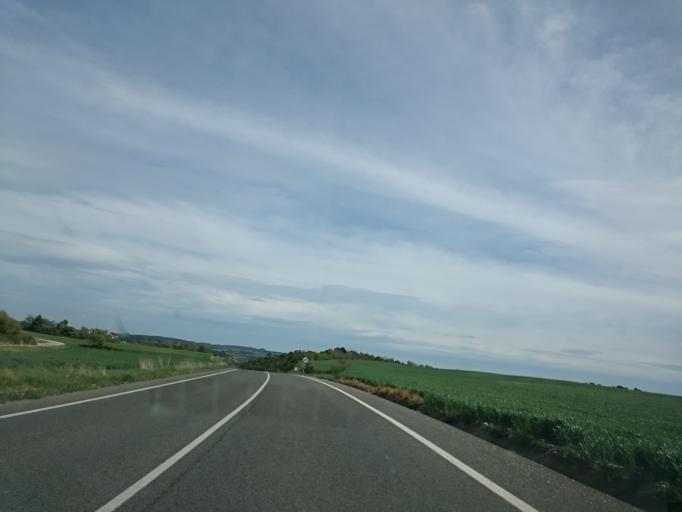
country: ES
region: Catalonia
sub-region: Provincia de Tarragona
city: Santa Coloma de Queralt
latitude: 41.5621
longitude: 1.3978
